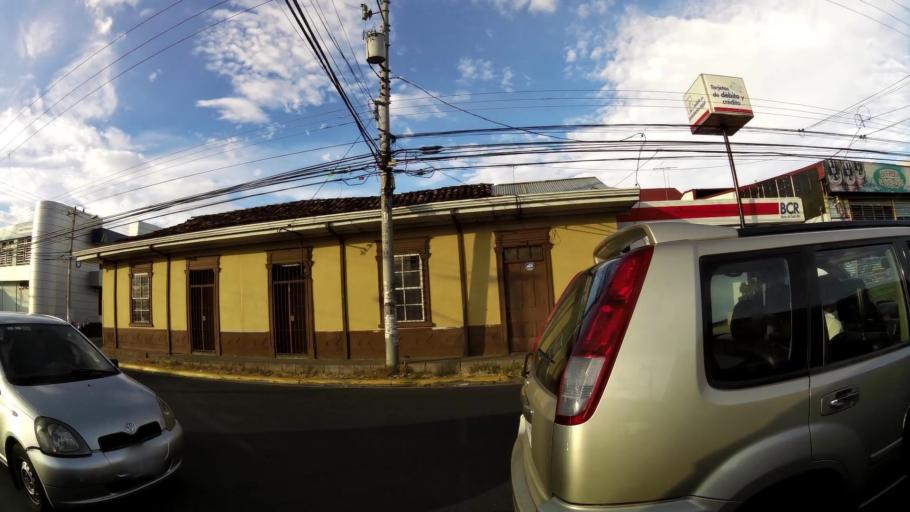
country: CR
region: Heredia
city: Llorente
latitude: 10.0012
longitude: -84.1538
